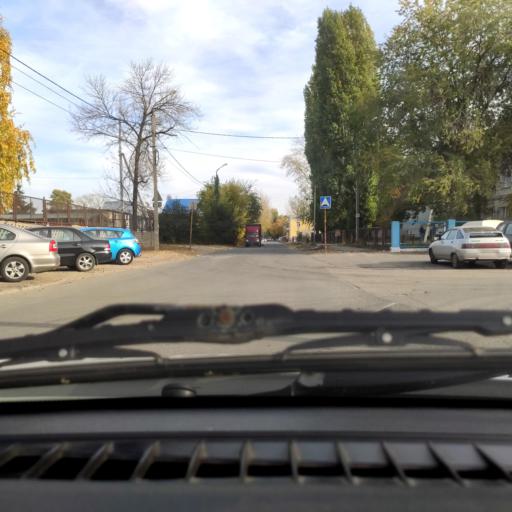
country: RU
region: Samara
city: Tol'yatti
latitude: 53.5248
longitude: 49.4187
